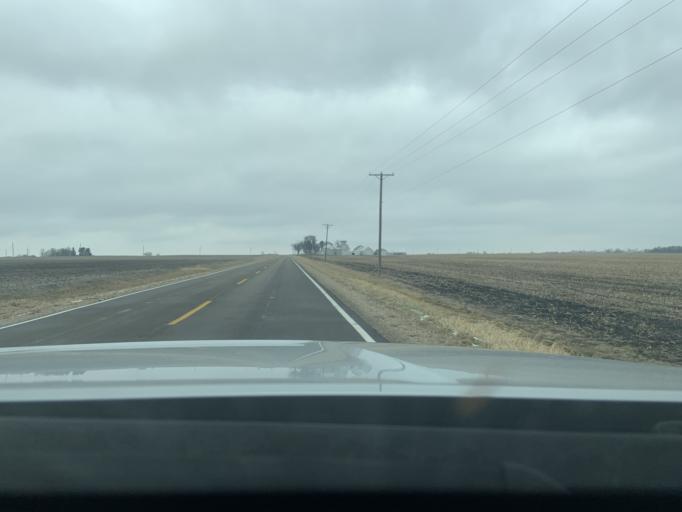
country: US
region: Illinois
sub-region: LaSalle County
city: Sheridan
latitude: 41.4516
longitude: -88.6152
